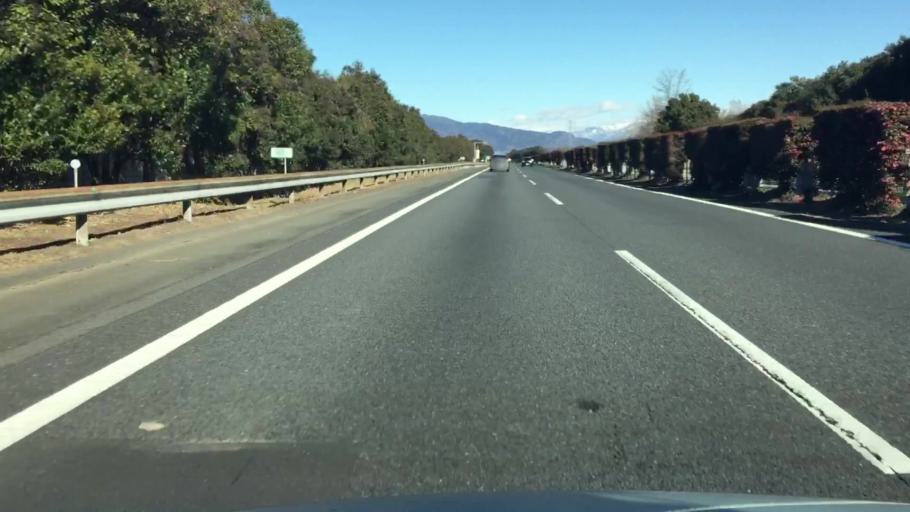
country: JP
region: Gunma
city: Kanekomachi
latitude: 36.4413
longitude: 139.0144
